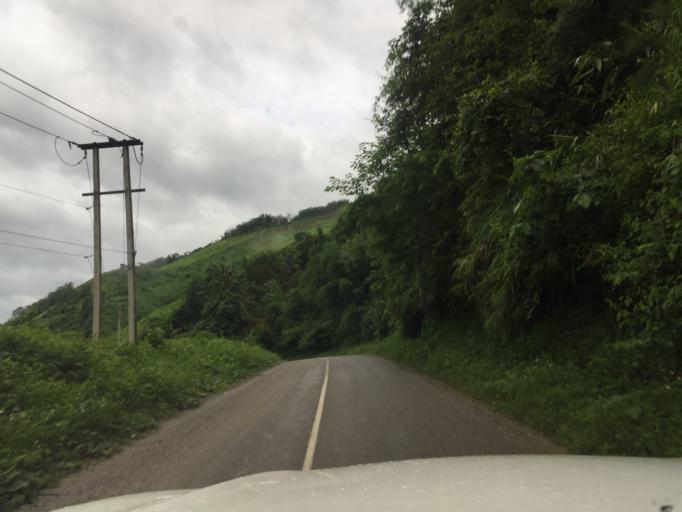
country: LA
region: Oudomxai
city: Muang La
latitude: 21.0051
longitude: 102.2332
